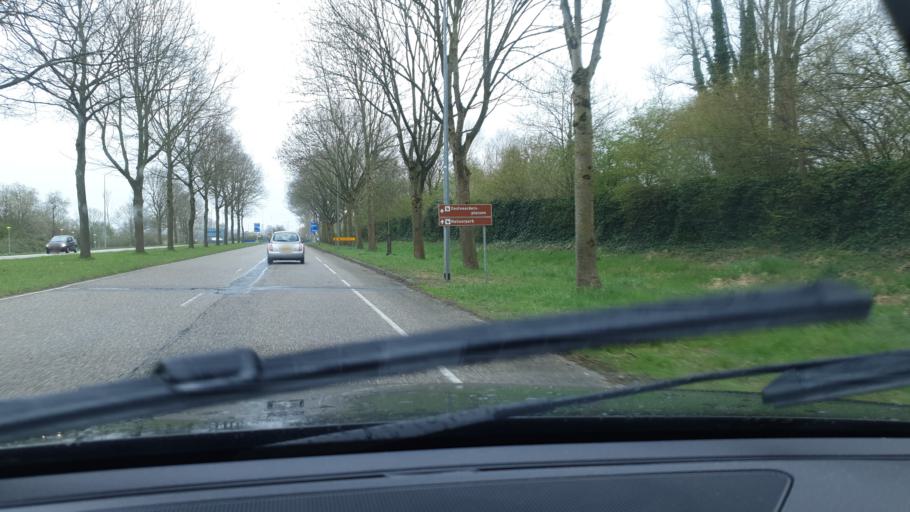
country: NL
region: Flevoland
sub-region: Gemeente Lelystad
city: Lelystad
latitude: 52.5023
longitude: 5.5108
